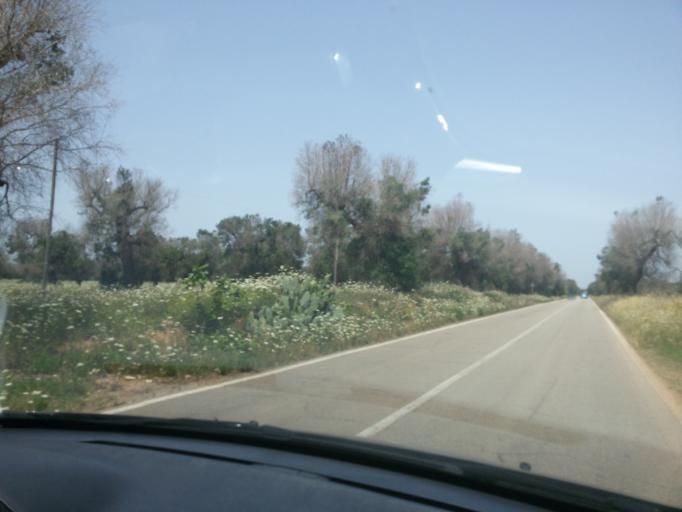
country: IT
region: Apulia
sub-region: Provincia di Lecce
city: Veglie
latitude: 40.3129
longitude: 17.9212
